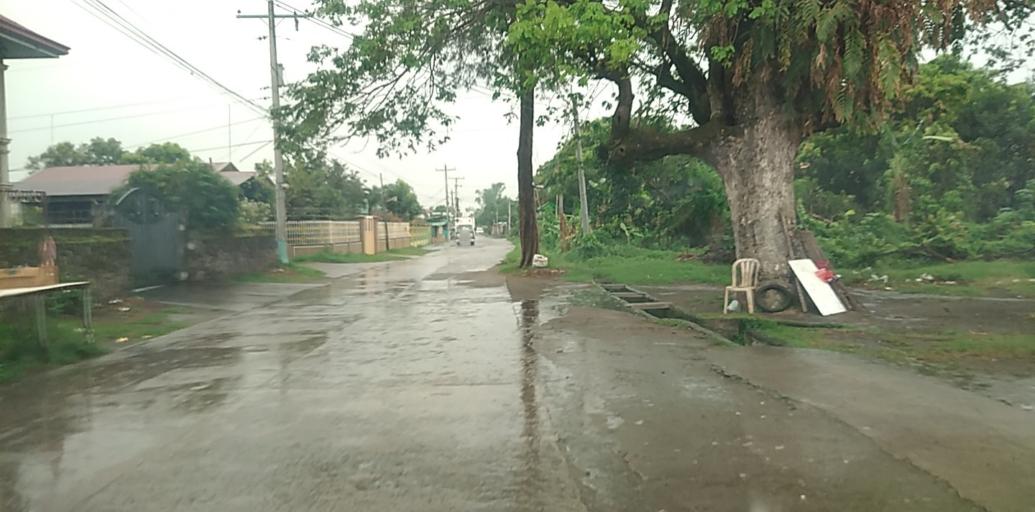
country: PH
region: Central Luzon
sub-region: Province of Pampanga
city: Arenas
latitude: 15.1721
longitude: 120.6839
